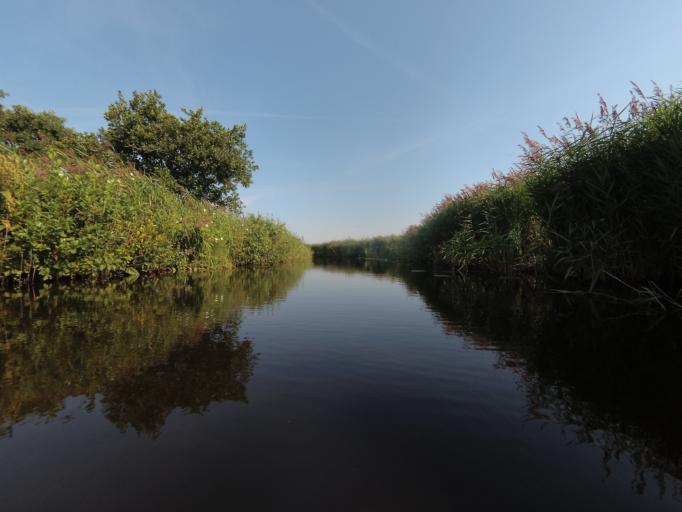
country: NL
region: Overijssel
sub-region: Gemeente Steenwijkerland
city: Sint Jansklooster
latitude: 52.6665
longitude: 6.0678
